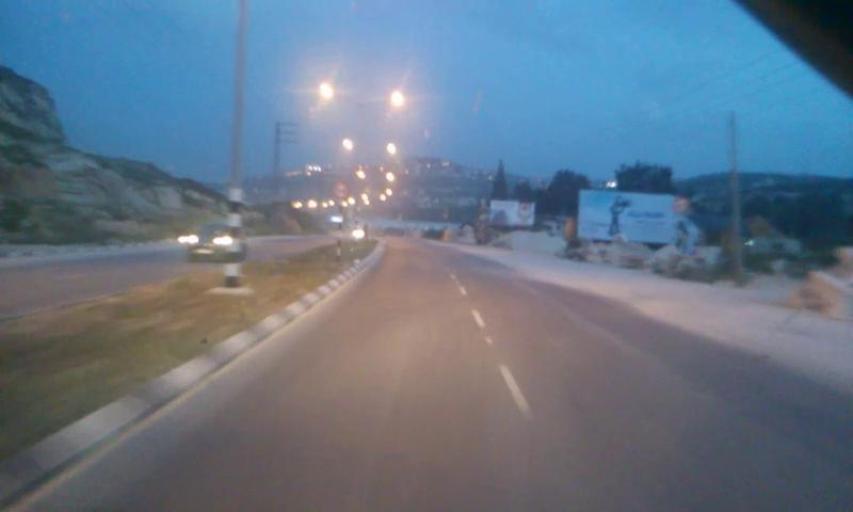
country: PS
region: West Bank
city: Dayr Sharaf
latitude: 32.2450
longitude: 35.1946
